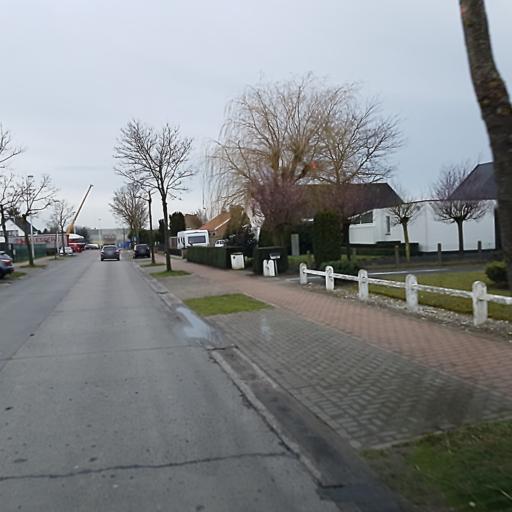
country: BE
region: Flanders
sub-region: Provincie Oost-Vlaanderen
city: Maldegem
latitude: 51.2026
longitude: 3.4668
